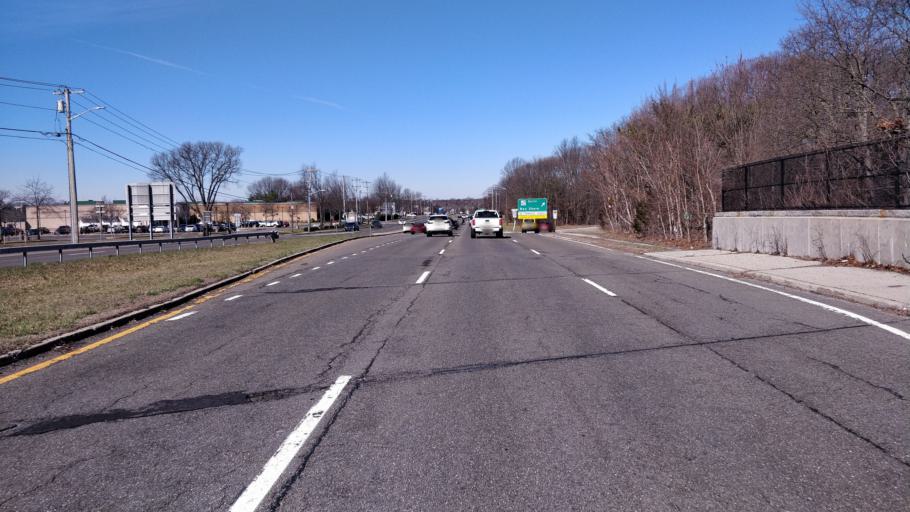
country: US
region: New York
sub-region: Suffolk County
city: Commack
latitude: 40.8398
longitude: -73.2814
